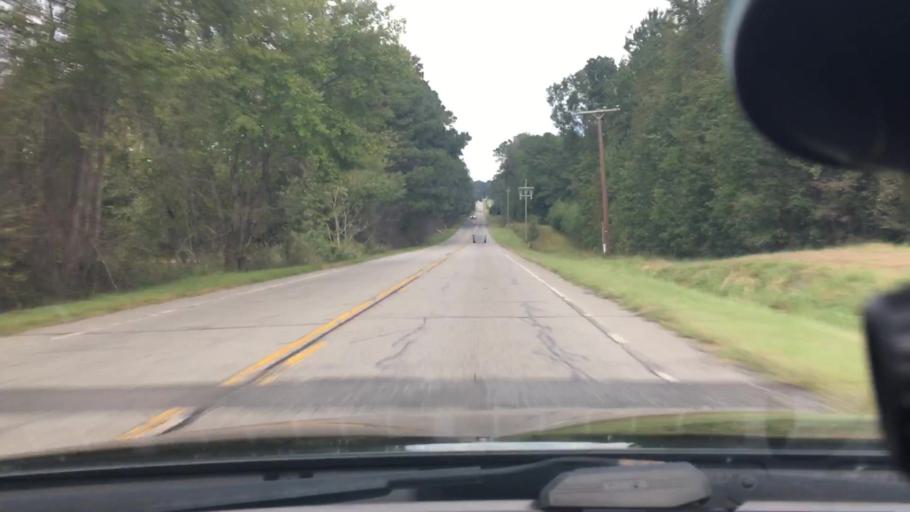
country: US
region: North Carolina
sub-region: Moore County
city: Carthage
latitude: 35.3499
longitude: -79.3574
